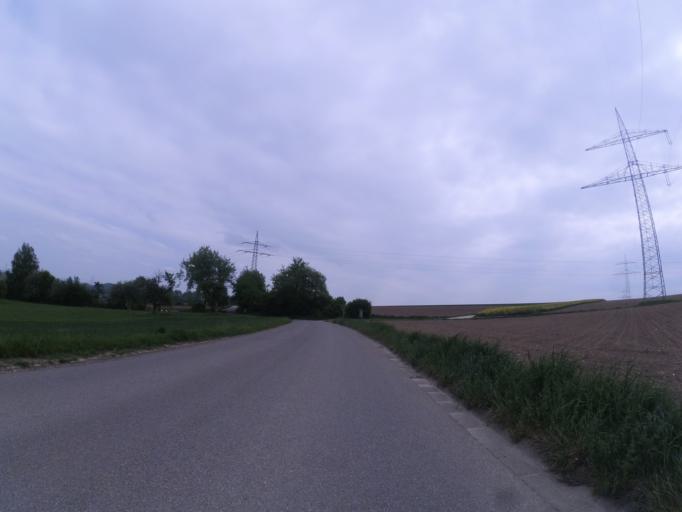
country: DE
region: Baden-Wuerttemberg
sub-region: Tuebingen Region
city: Staig
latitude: 48.3094
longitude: 10.0060
